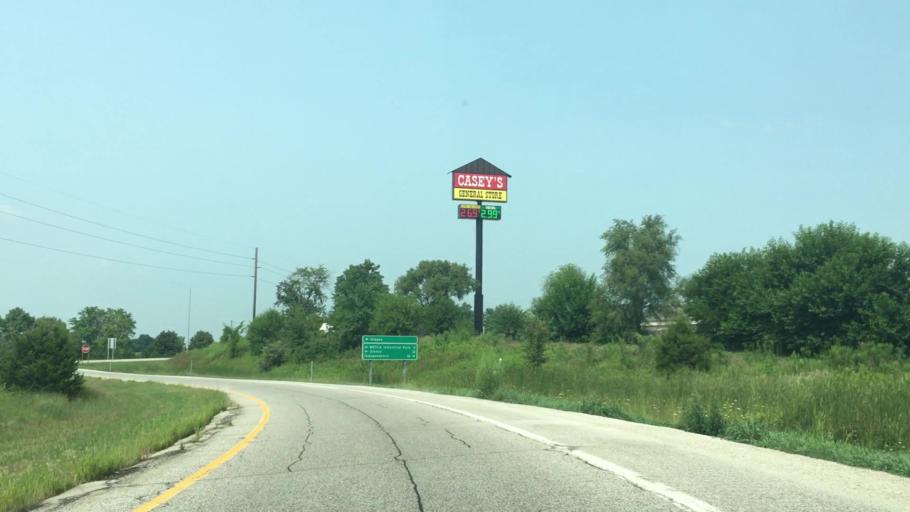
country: US
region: Iowa
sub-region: Benton County
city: Urbana
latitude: 42.2453
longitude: -91.8893
